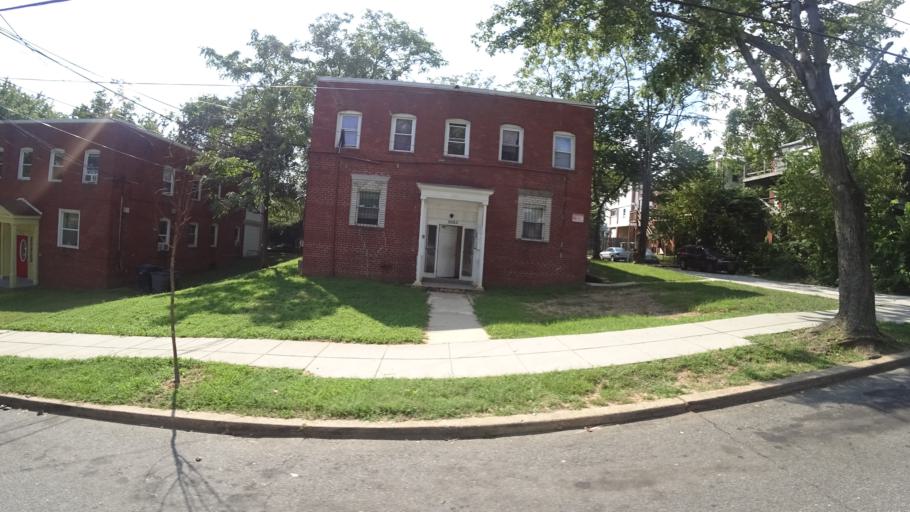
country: US
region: Maryland
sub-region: Prince George's County
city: Hillcrest Heights
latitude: 38.8508
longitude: -76.9680
